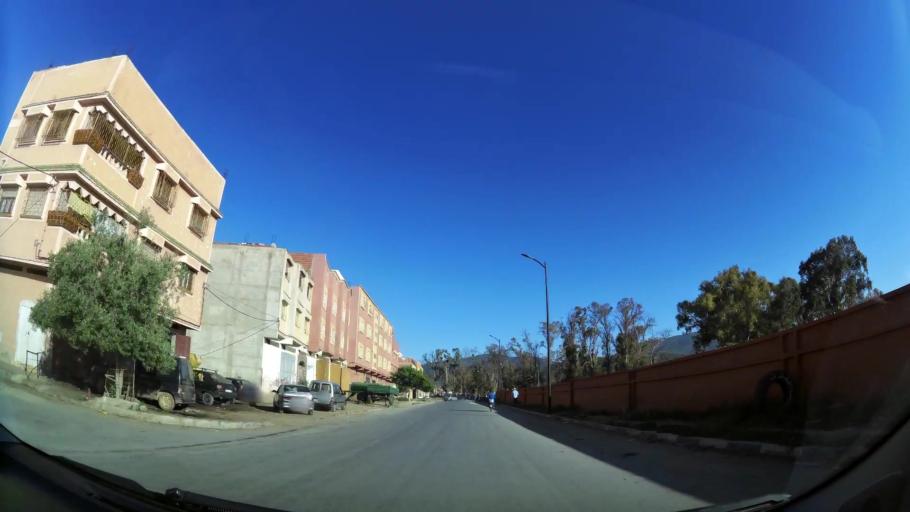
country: MA
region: Oriental
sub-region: Berkane-Taourirt
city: Berkane
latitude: 34.9248
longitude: -2.3406
